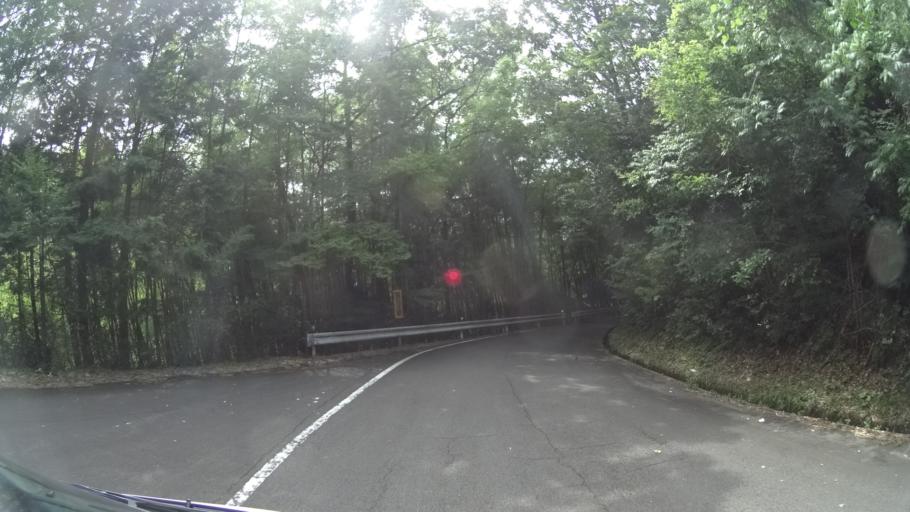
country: JP
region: Kyoto
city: Fukuchiyama
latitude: 35.3677
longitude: 135.1745
